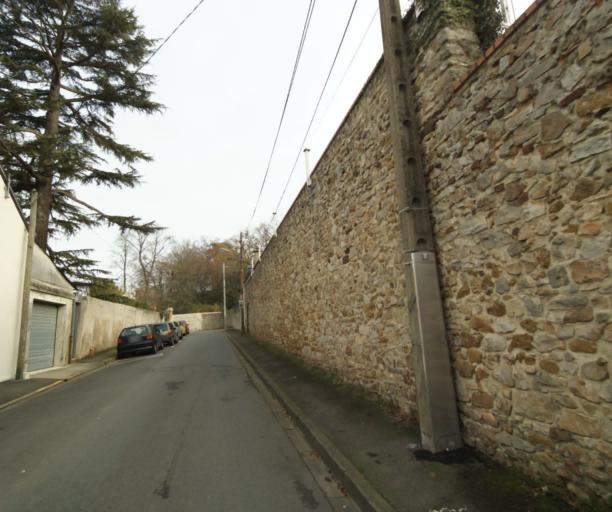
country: FR
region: Pays de la Loire
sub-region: Departement de la Sarthe
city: Le Mans
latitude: 48.0064
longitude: 0.2086
